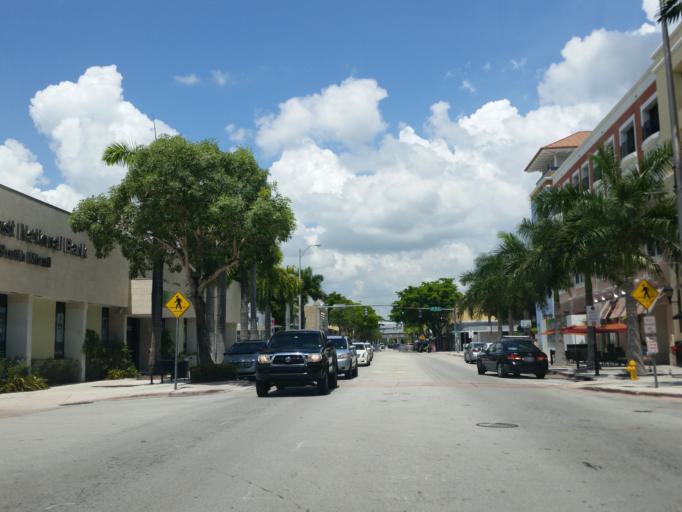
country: US
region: Florida
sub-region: Miami-Dade County
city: South Miami
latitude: 25.7044
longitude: -80.2863
